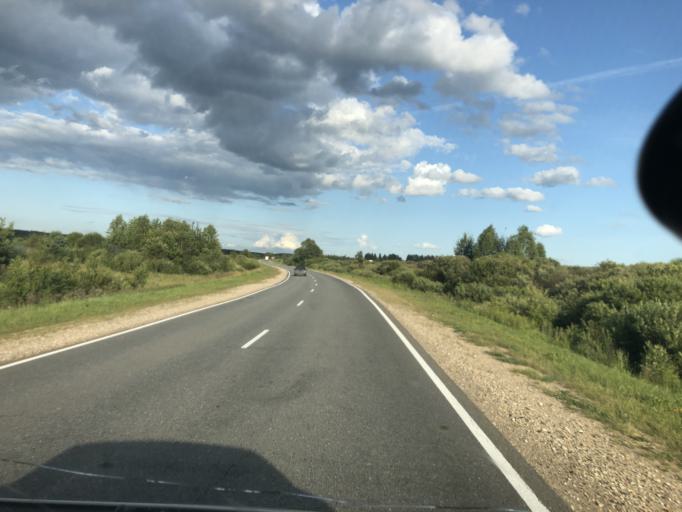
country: RU
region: Kaluga
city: Yukhnov
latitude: 54.7003
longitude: 35.2745
